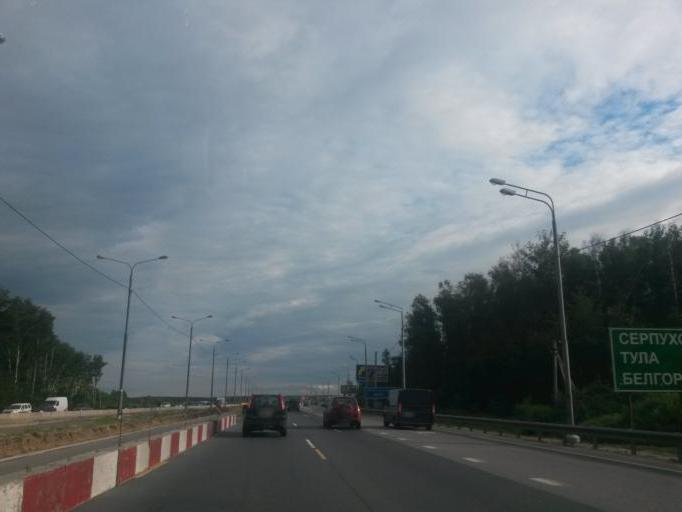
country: RU
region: Moskovskaya
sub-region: Podol'skiy Rayon
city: Podol'sk
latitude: 55.3966
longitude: 37.6048
